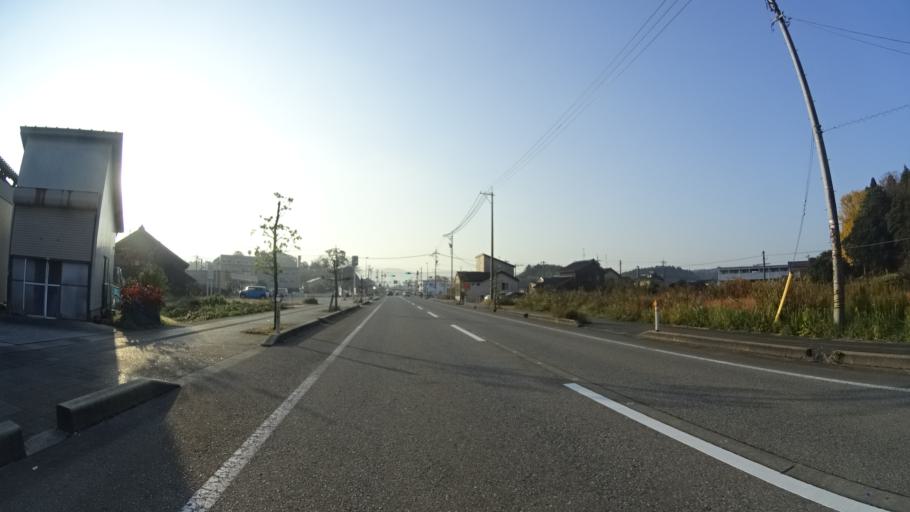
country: JP
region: Ishikawa
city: Nanao
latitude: 37.0496
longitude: 136.9568
